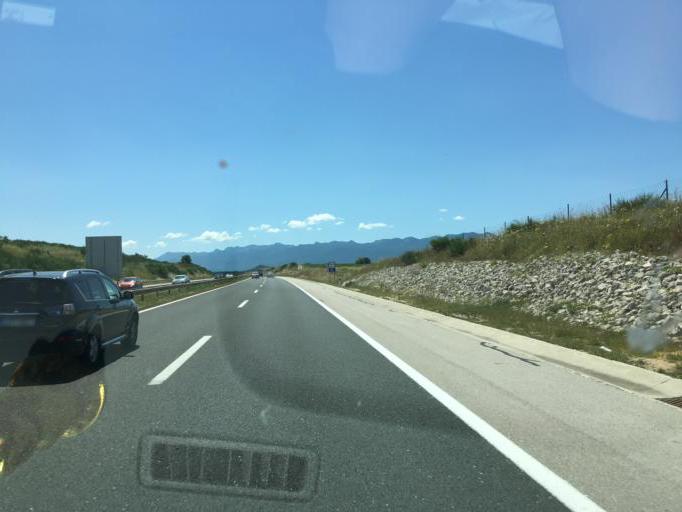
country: HR
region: Licko-Senjska
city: Gospic
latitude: 44.5613
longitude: 15.4277
